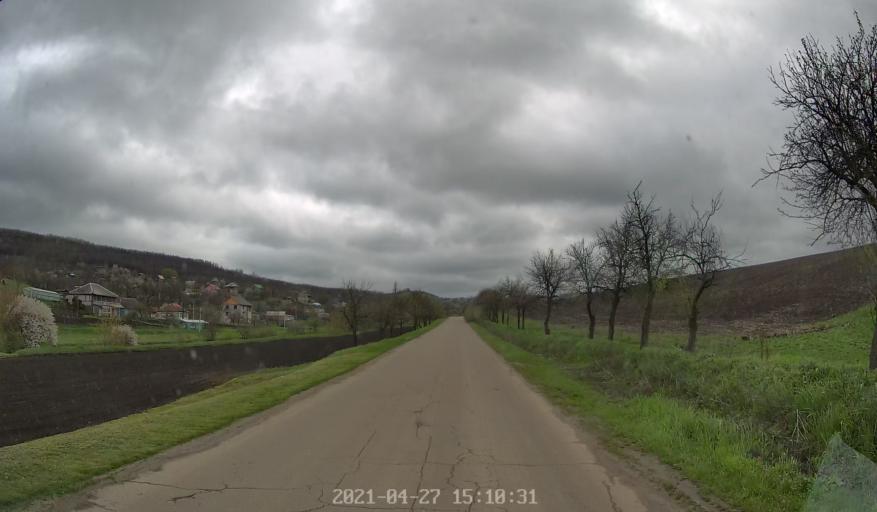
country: MD
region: Chisinau
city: Vadul lui Voda
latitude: 47.0396
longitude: 29.0326
